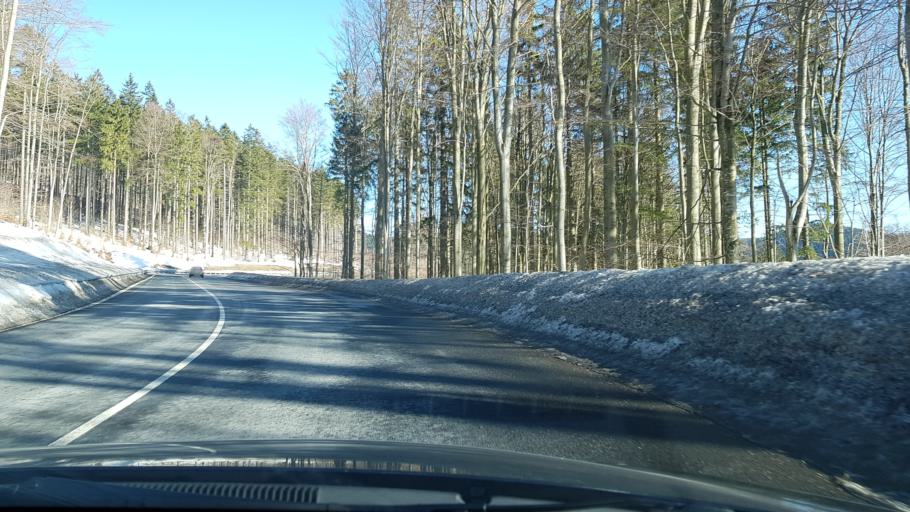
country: CZ
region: Olomoucky
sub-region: Okres Sumperk
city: Loucna nad Desnou
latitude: 50.1126
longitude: 17.1444
